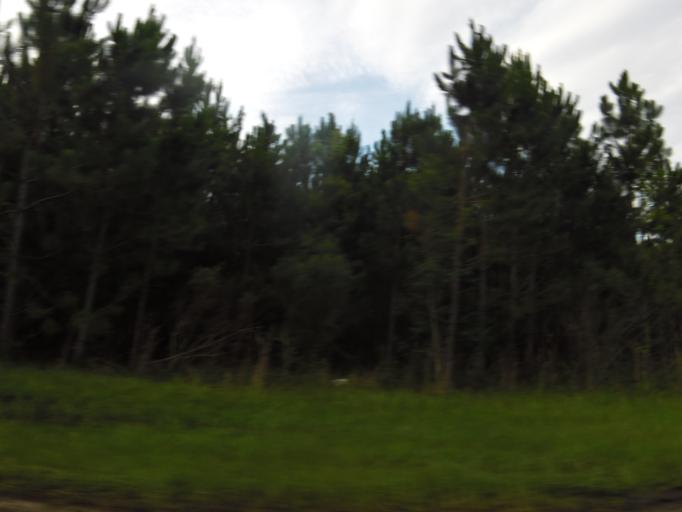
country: US
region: Florida
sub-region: Duval County
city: Jacksonville
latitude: 30.3413
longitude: -81.7751
